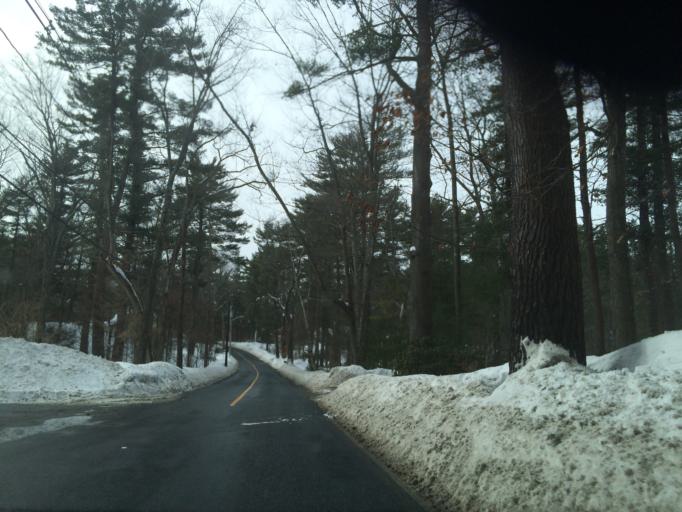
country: US
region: Massachusetts
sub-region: Middlesex County
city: Weston
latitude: 42.3872
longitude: -71.3071
